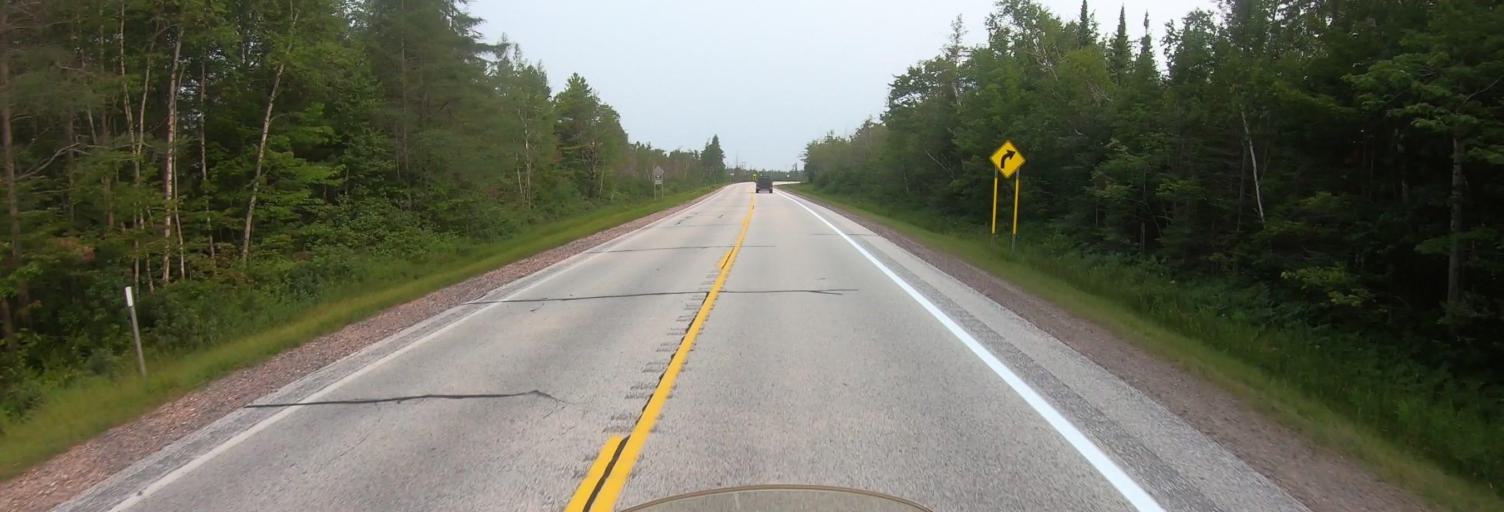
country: US
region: Michigan
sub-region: Luce County
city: Newberry
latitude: 46.5648
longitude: -85.0311
